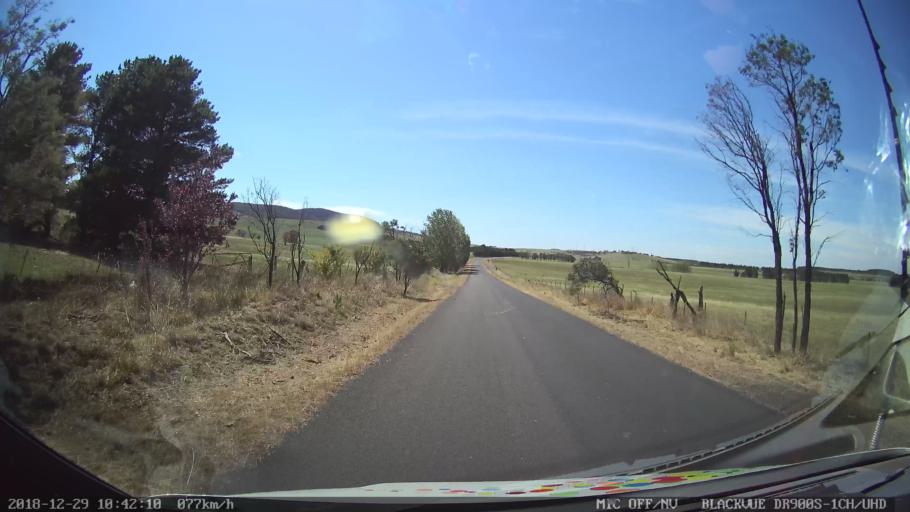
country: AU
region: New South Wales
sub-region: Palerang
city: Bungendore
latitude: -35.0307
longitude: 149.5273
